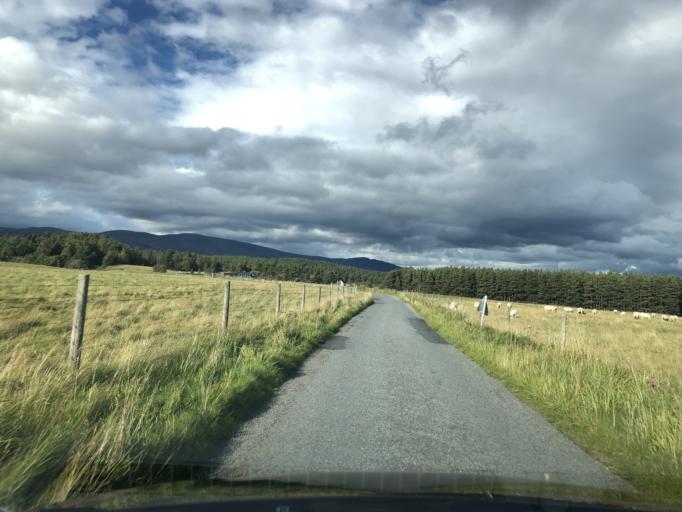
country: GB
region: Scotland
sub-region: Highland
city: Aviemore
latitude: 57.1064
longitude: -3.8872
